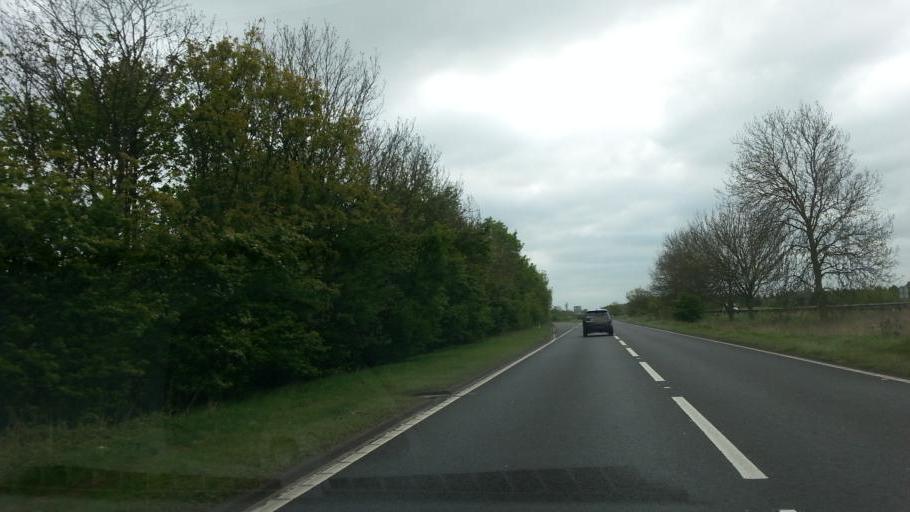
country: GB
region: England
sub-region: District of Rutland
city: Clipsham
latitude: 52.7041
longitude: -0.5832
